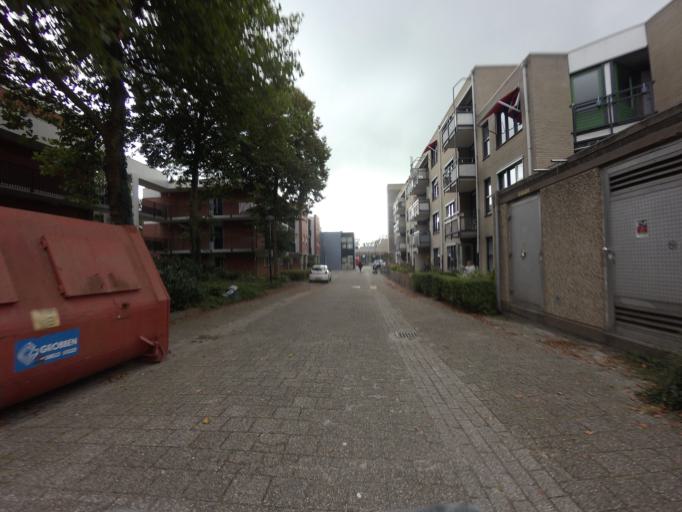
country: NL
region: Overijssel
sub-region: Gemeente Enschede
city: Enschede
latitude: 52.1947
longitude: 6.9019
